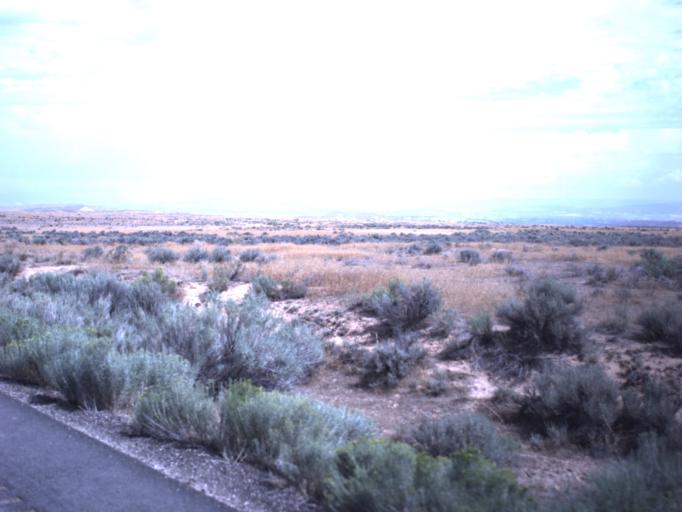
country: US
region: Utah
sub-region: Uintah County
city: Naples
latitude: 40.2458
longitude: -109.4203
